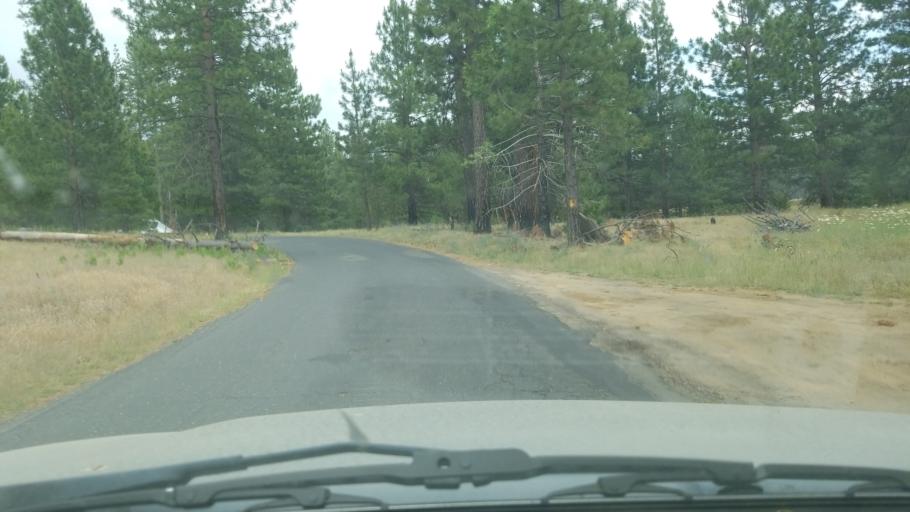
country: US
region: California
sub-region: Mariposa County
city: Yosemite Valley
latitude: 37.8495
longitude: -119.8609
